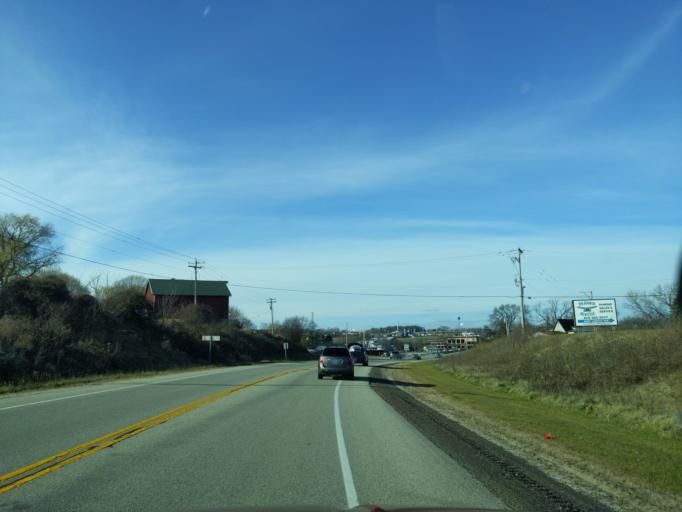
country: US
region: Wisconsin
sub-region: Rock County
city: Edgerton
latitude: 42.8277
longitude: -89.0188
